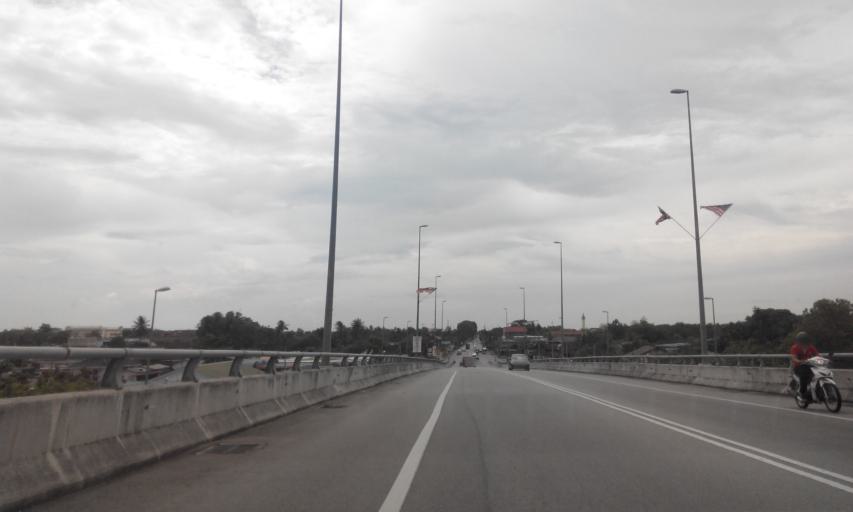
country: MY
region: Perak
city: Parit Buntar
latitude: 5.1320
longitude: 100.4848
